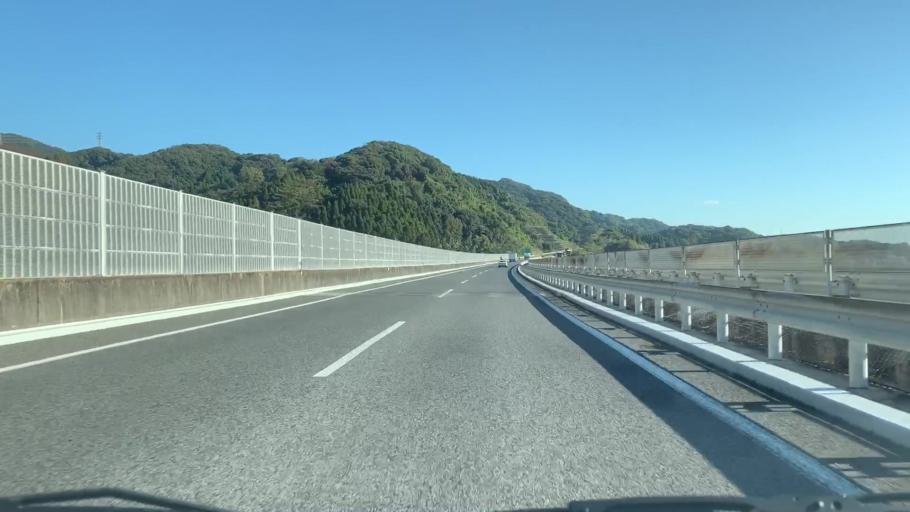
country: JP
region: Saga Prefecture
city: Saga-shi
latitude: 33.2958
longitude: 130.1723
